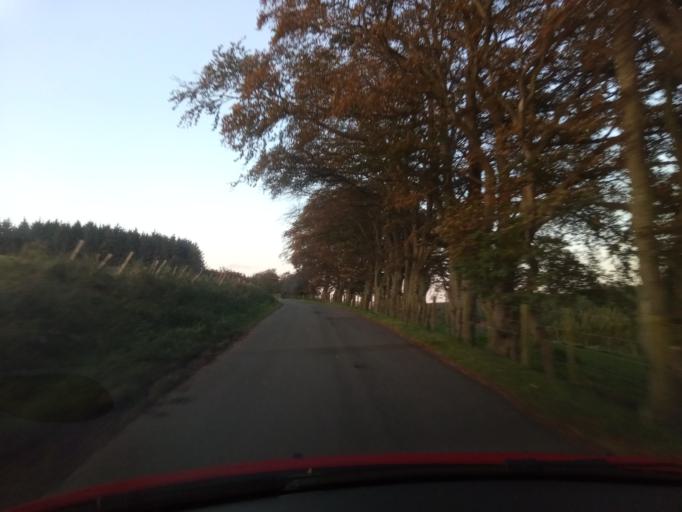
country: GB
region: Scotland
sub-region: Fife
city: Pathhead
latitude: 55.7925
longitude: -2.8901
